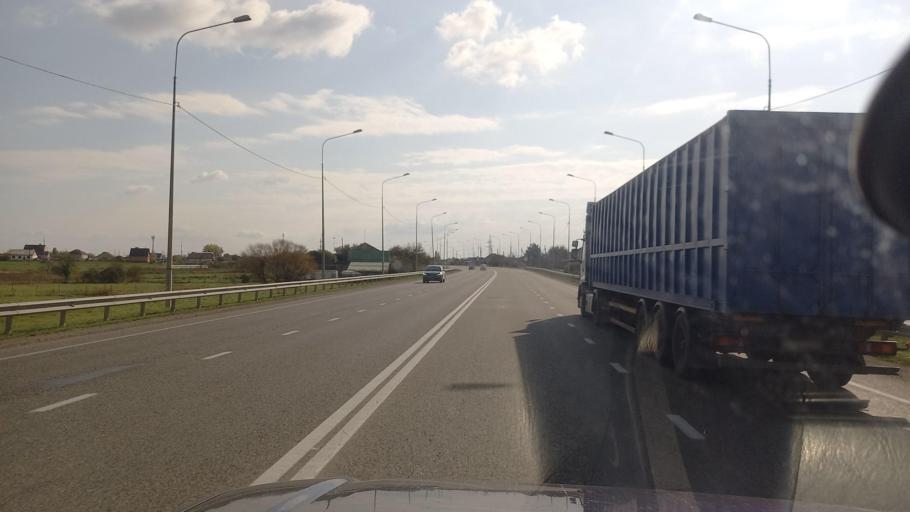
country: RU
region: Krasnodarskiy
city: Novoukrainskiy
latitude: 44.8995
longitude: 38.0402
